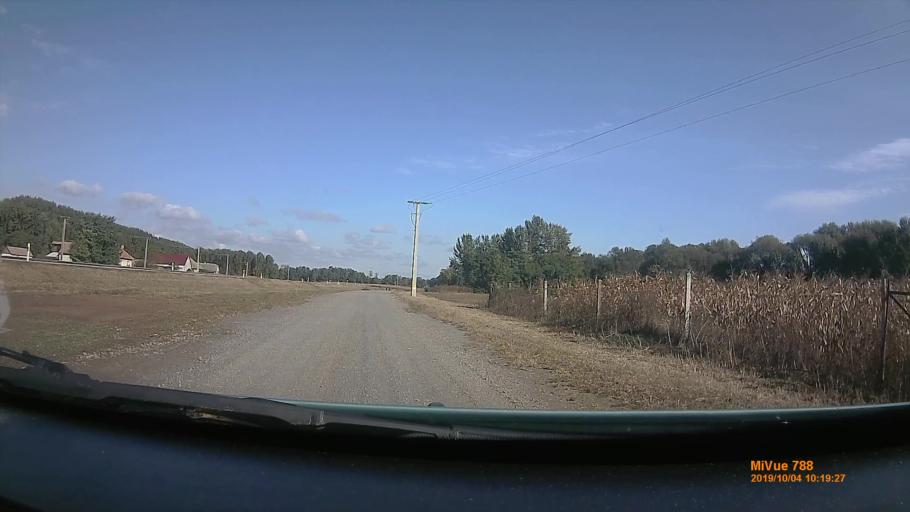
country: HU
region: Szabolcs-Szatmar-Bereg
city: Nyirtelek
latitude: 47.9617
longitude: 21.6571
